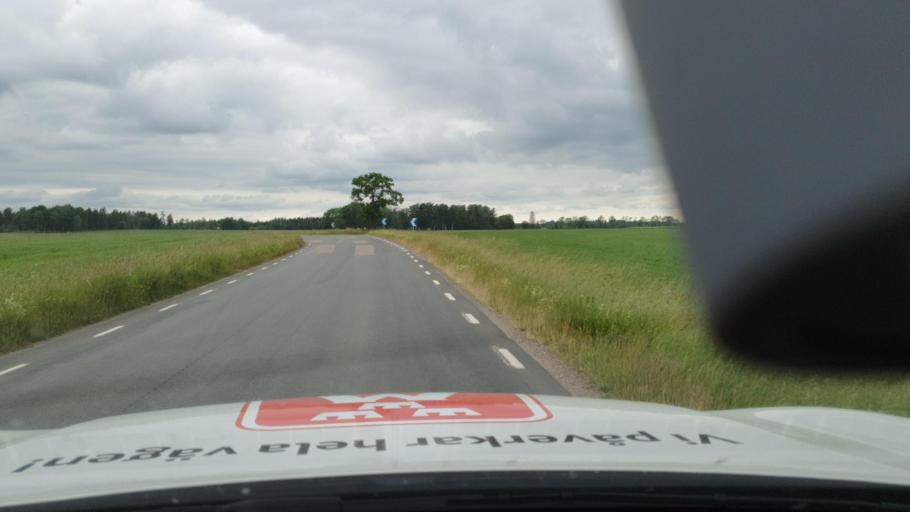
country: SE
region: Vaestra Goetaland
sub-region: Tidaholms Kommun
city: Olofstorp
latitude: 58.3009
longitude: 14.0442
